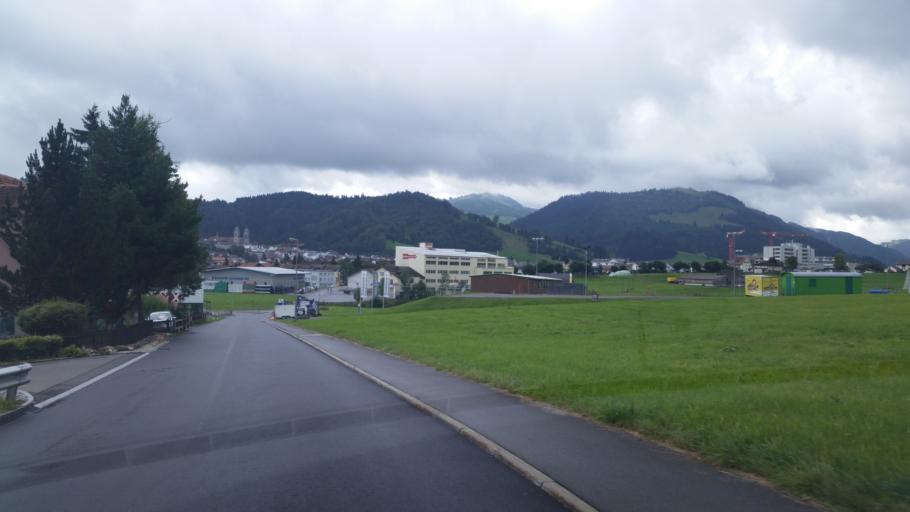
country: CH
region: Schwyz
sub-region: Bezirk Einsiedeln
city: Einsiedeln
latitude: 47.1377
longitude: 8.7403
